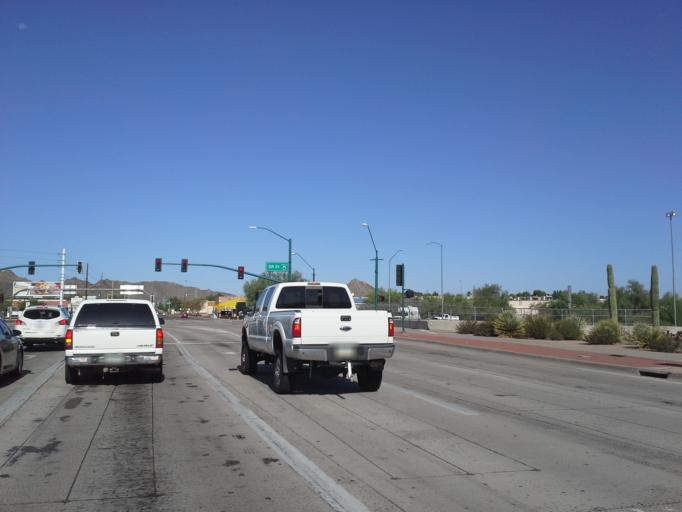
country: US
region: Arizona
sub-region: Maricopa County
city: Paradise Valley
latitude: 33.5826
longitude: -112.0091
